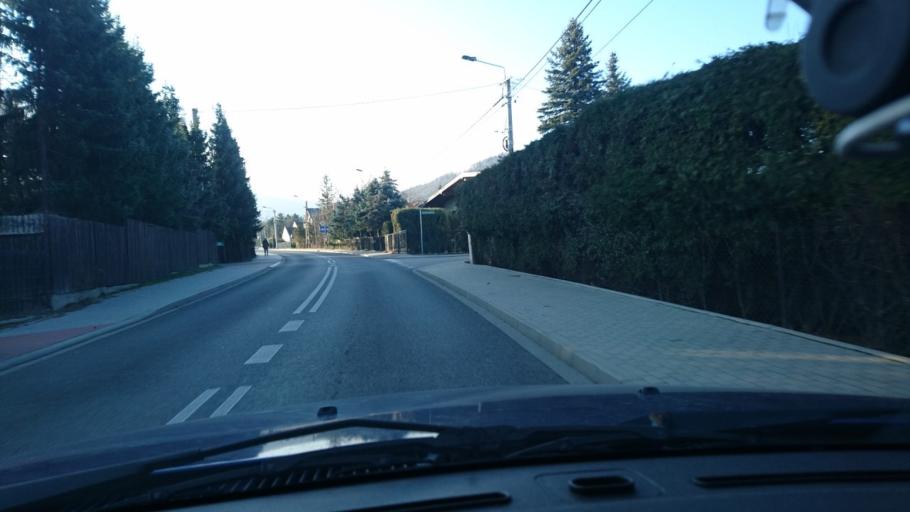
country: PL
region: Silesian Voivodeship
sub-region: Powiat bielski
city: Jaworze
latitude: 49.7923
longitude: 18.9830
